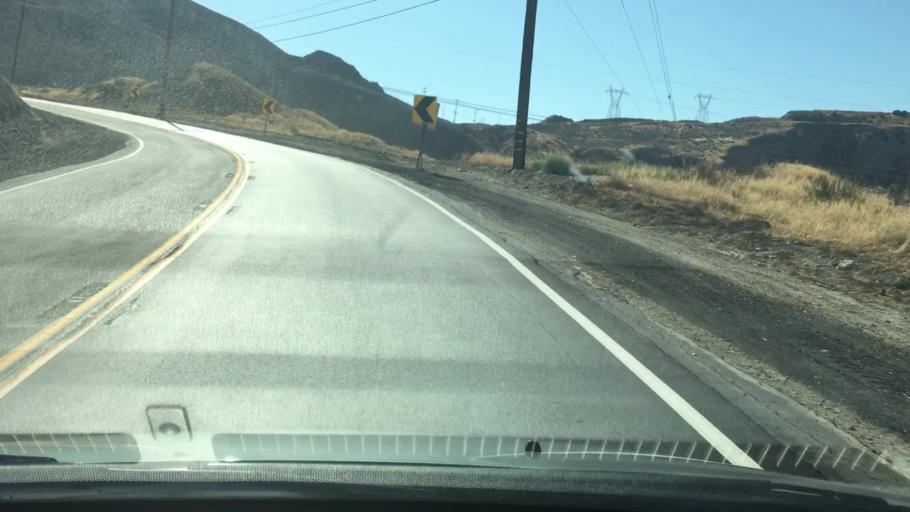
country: US
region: California
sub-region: Los Angeles County
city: Agua Dulce
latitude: 34.4730
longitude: -118.4411
